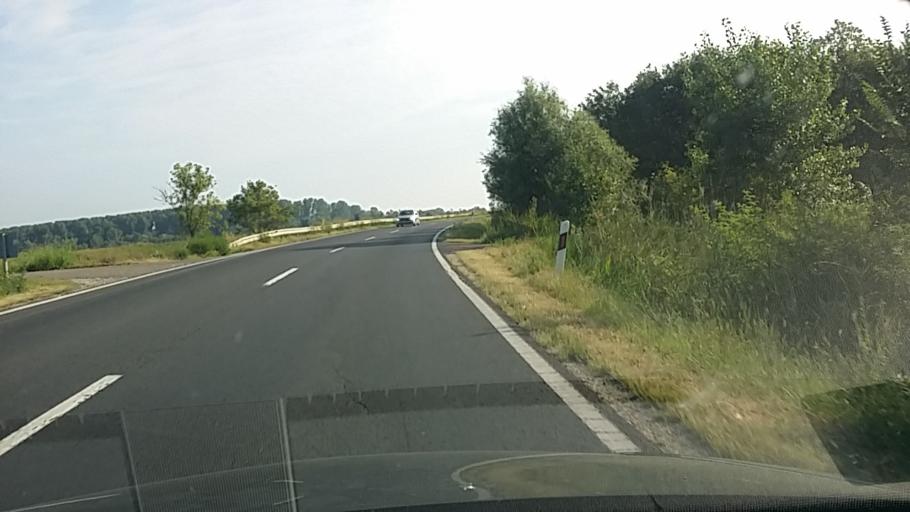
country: HU
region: Jasz-Nagykun-Szolnok
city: Kunszentmarton
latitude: 46.8718
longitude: 20.3120
